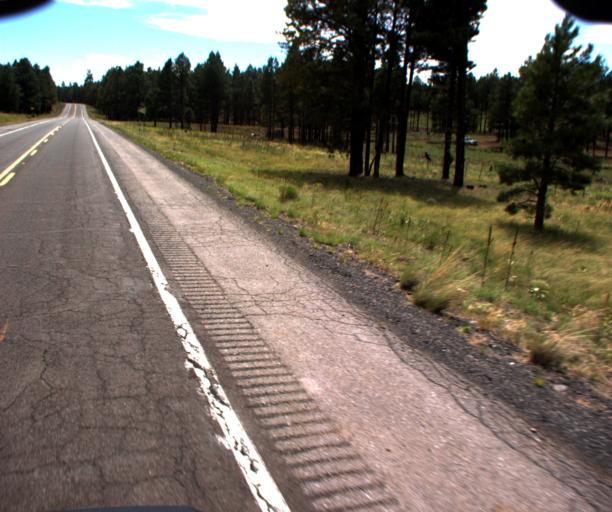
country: US
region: Arizona
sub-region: Coconino County
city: Parks
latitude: 35.4406
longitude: -111.7617
